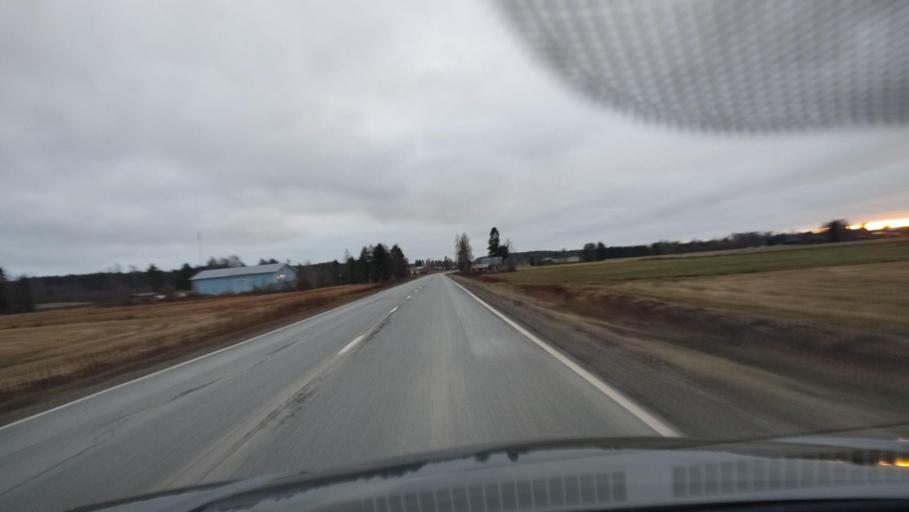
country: FI
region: Southern Ostrobothnia
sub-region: Suupohja
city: Kauhajoki
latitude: 62.3645
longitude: 22.0739
